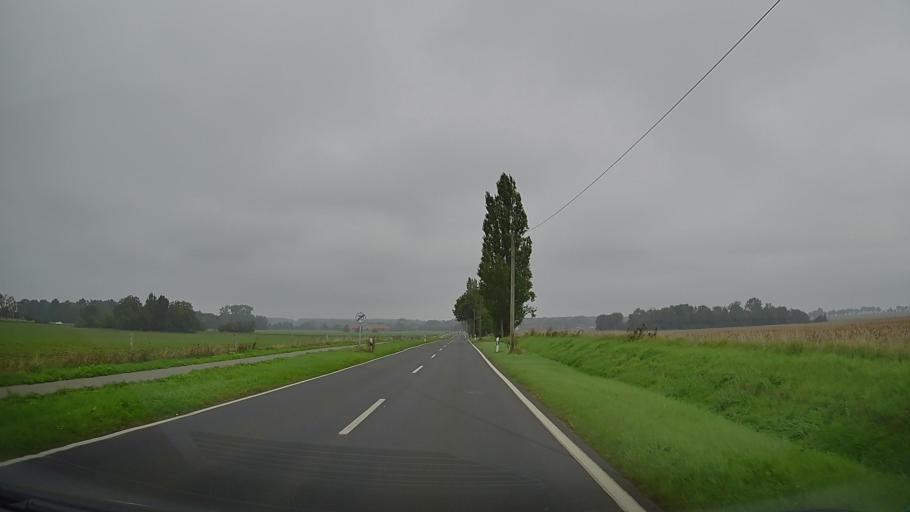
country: DE
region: Mecklenburg-Vorpommern
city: Neubukow
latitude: 54.0654
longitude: 11.6272
